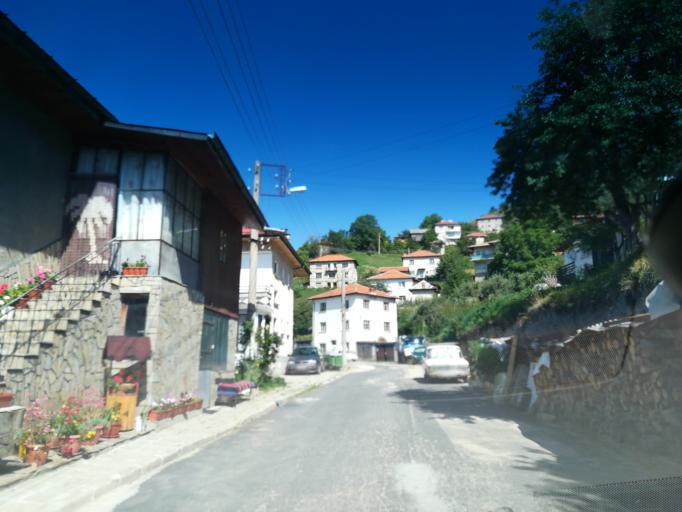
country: BG
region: Smolyan
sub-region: Obshtina Smolyan
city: Smolyan
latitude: 41.6585
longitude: 24.8314
